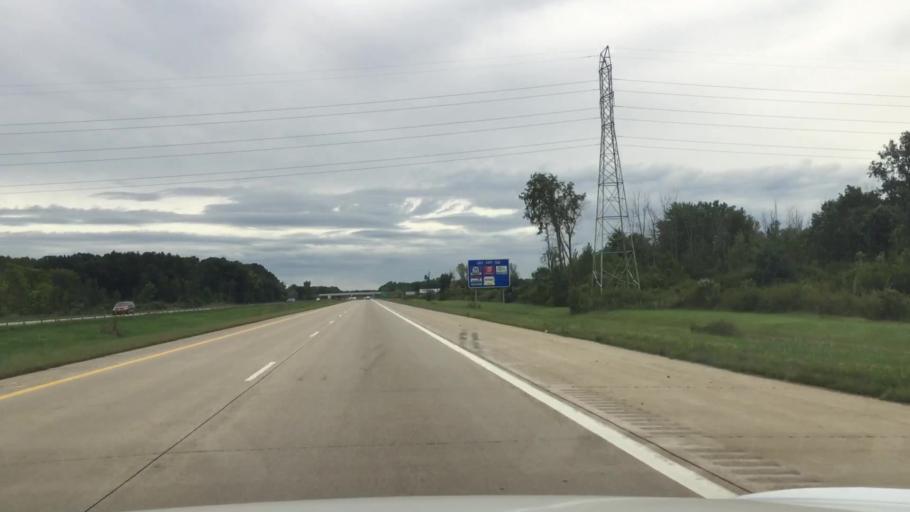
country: US
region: Michigan
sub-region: Saint Clair County
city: Marysville
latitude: 42.9289
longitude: -82.5067
